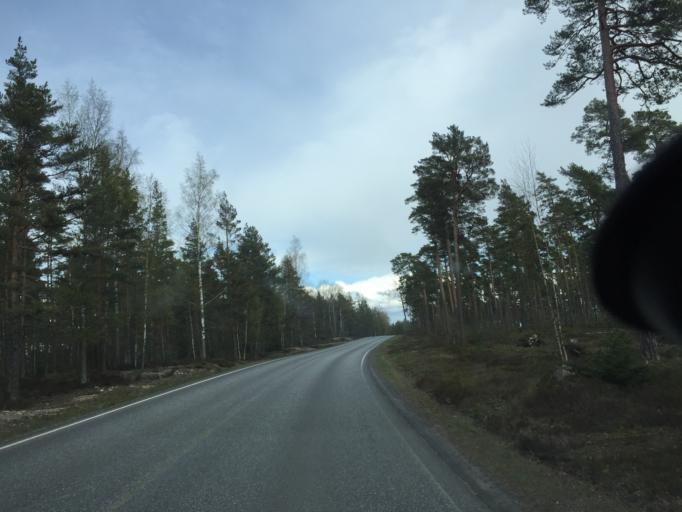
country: FI
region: Varsinais-Suomi
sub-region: Salo
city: Pernioe
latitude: 60.0084
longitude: 23.1234
